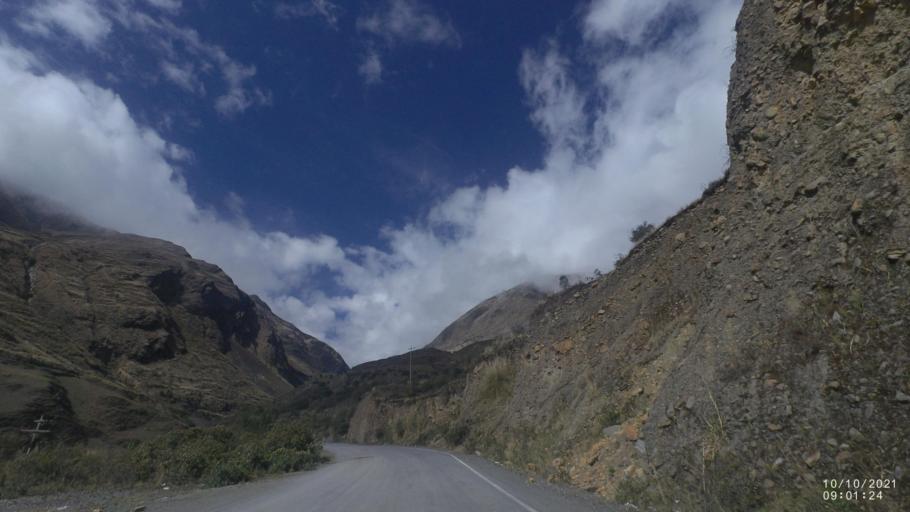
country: BO
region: La Paz
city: Quime
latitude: -17.0013
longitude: -67.2663
